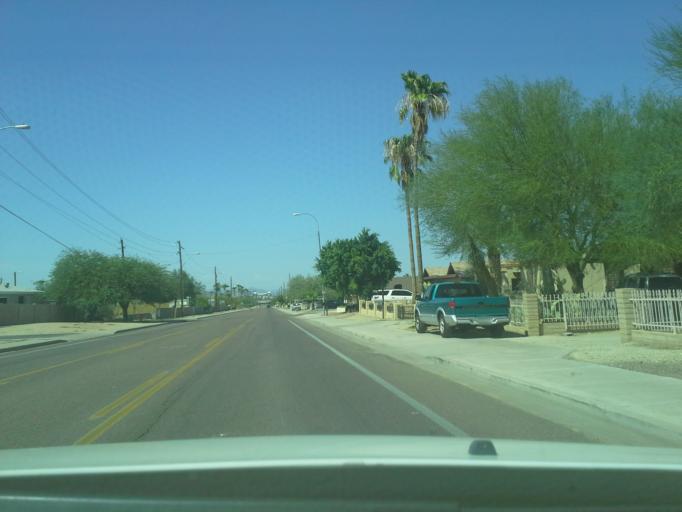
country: US
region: Arizona
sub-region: Maricopa County
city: Phoenix
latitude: 33.3681
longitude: -112.0659
